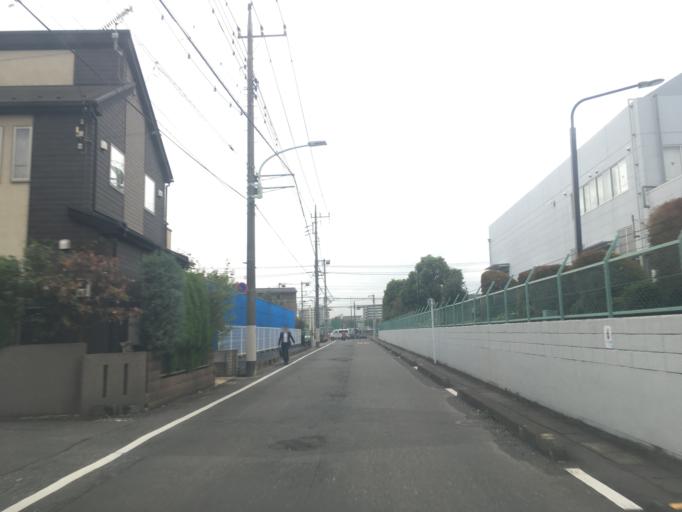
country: JP
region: Tokyo
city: Higashimurayama-shi
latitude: 35.7576
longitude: 139.4602
